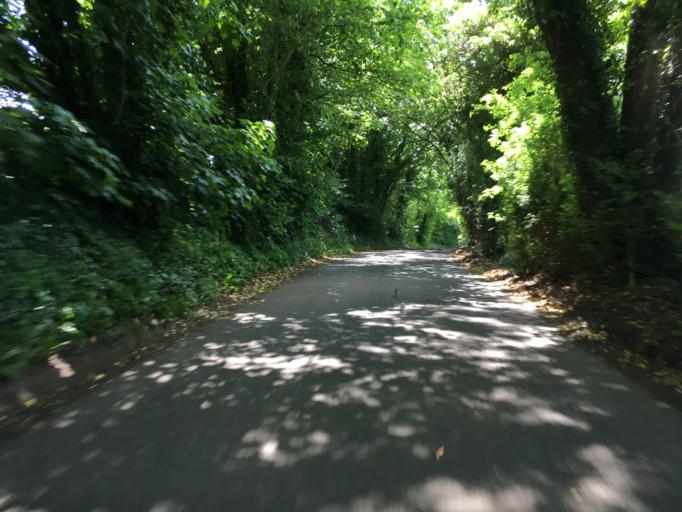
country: GB
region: England
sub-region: Gloucestershire
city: Stroud
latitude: 51.7519
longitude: -2.2203
